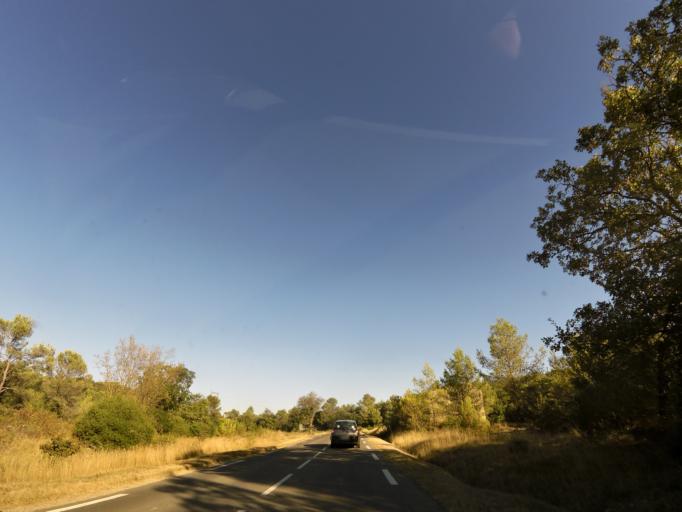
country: FR
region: Languedoc-Roussillon
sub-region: Departement du Gard
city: Sommieres
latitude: 43.8271
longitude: 4.0472
